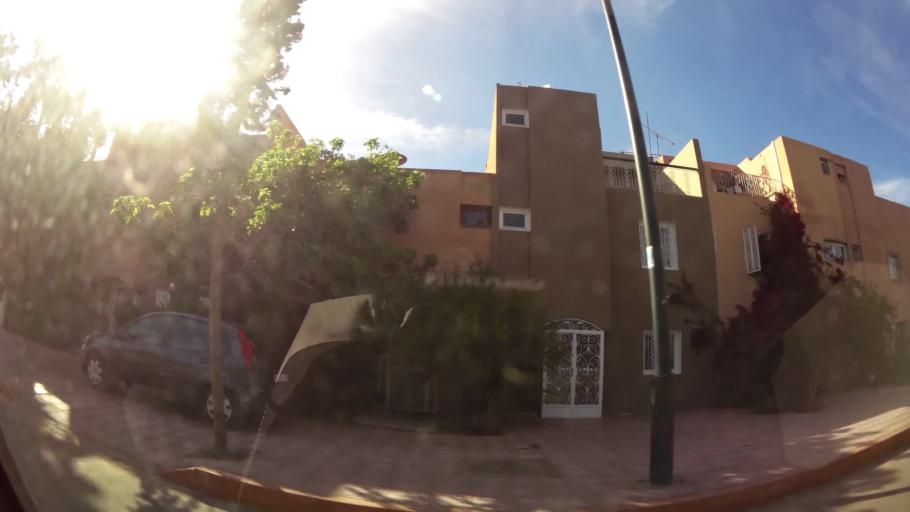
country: MA
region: Marrakech-Tensift-Al Haouz
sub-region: Marrakech
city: Marrakesh
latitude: 31.6582
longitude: -8.0104
